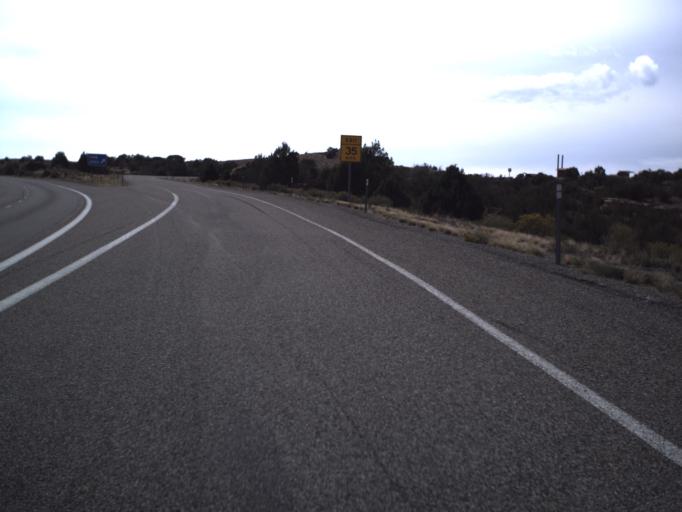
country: US
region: Colorado
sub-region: Mesa County
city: Loma
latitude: 39.1893
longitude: -109.1116
